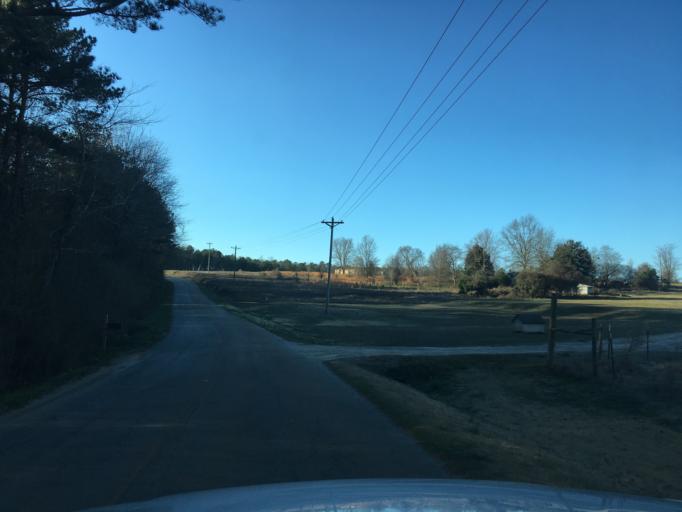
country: US
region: Georgia
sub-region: Carroll County
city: Carrollton
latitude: 33.4395
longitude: -85.1186
